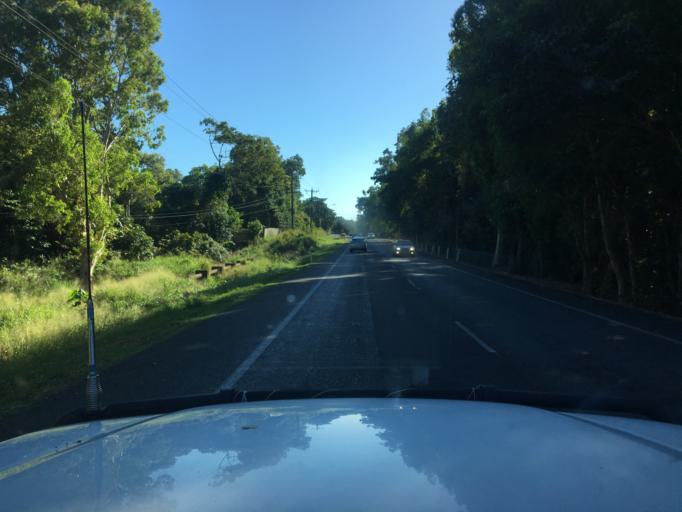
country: AU
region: Queensland
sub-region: Cairns
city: Trinity Beach
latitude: -16.7788
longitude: 145.6745
